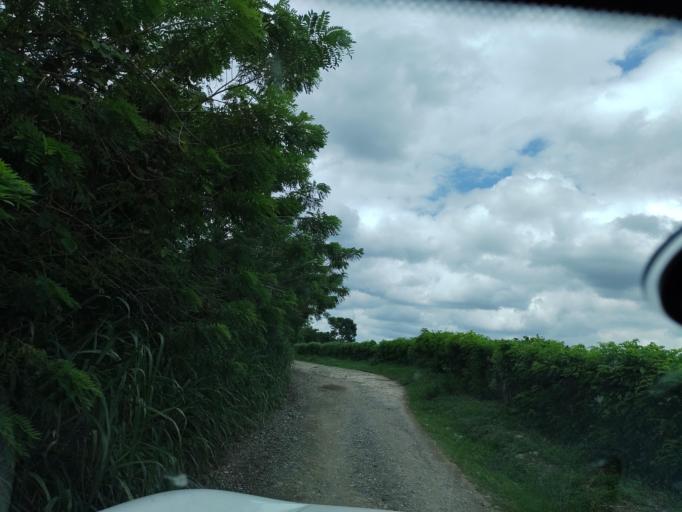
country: MX
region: Veracruz
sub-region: Martinez de la Torre
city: El Progreso
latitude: 20.1116
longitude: -97.0215
